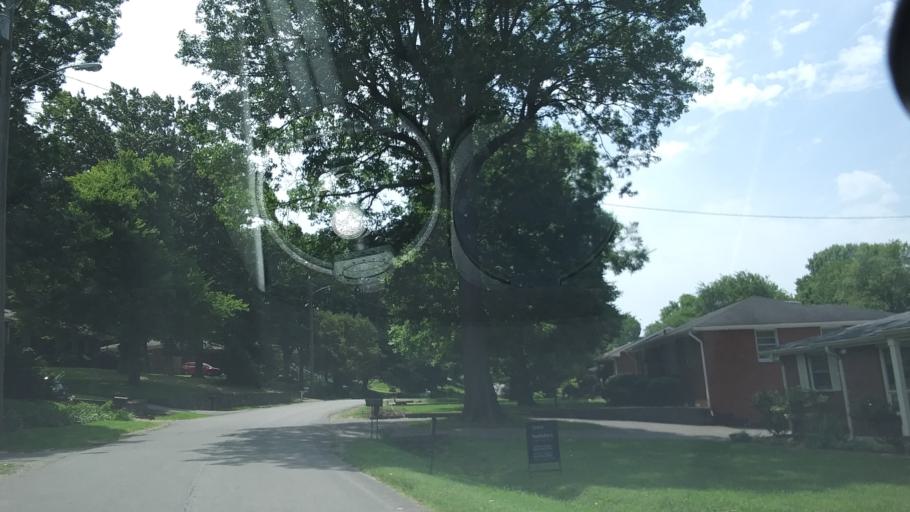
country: US
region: Tennessee
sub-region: Davidson County
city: Belle Meade
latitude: 36.1535
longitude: -86.8798
